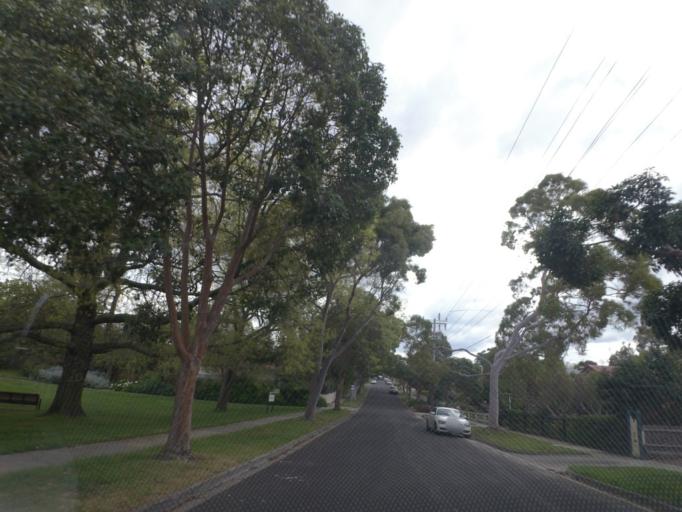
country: AU
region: Victoria
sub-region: Whitehorse
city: Box Hill
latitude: -37.8262
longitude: 145.1260
